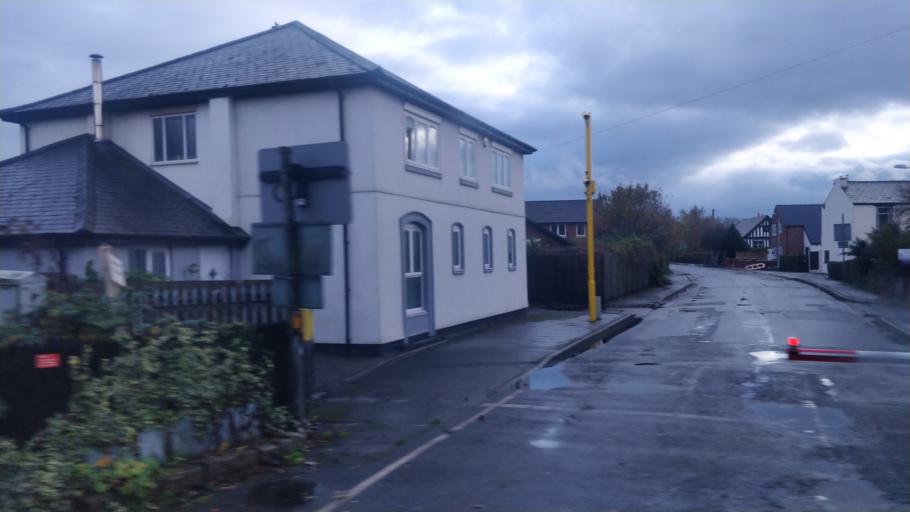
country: GB
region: England
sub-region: Lancashire
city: Banks
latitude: 53.6238
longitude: -2.9147
